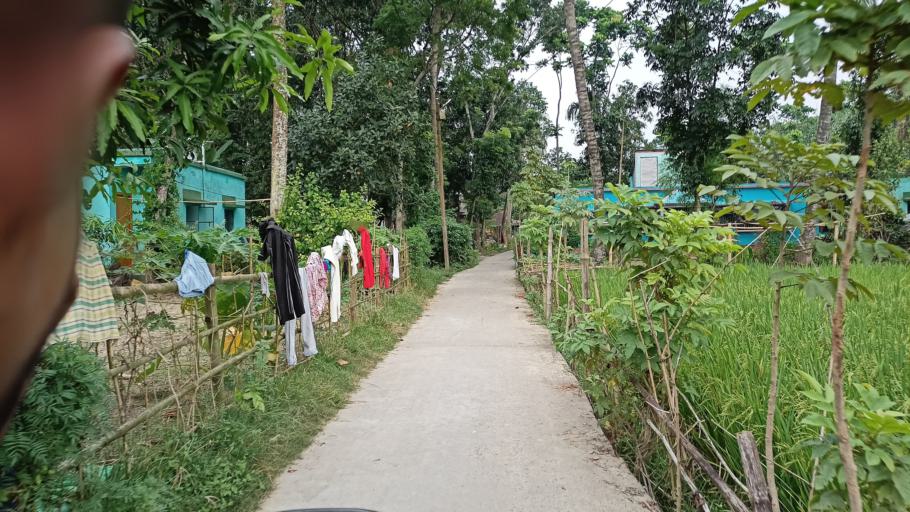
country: IN
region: West Bengal
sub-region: North 24 Parganas
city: Bangaon
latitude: 23.0645
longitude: 88.8189
